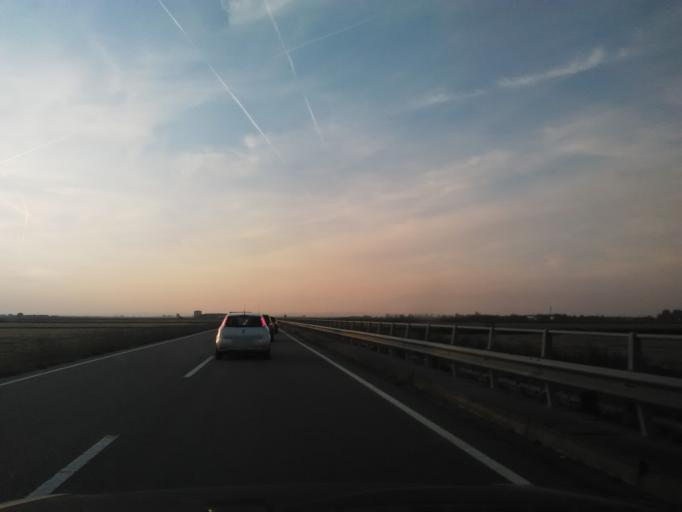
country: IT
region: Piedmont
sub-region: Provincia di Vercelli
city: Olcenengo
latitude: 45.3366
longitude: 8.3009
